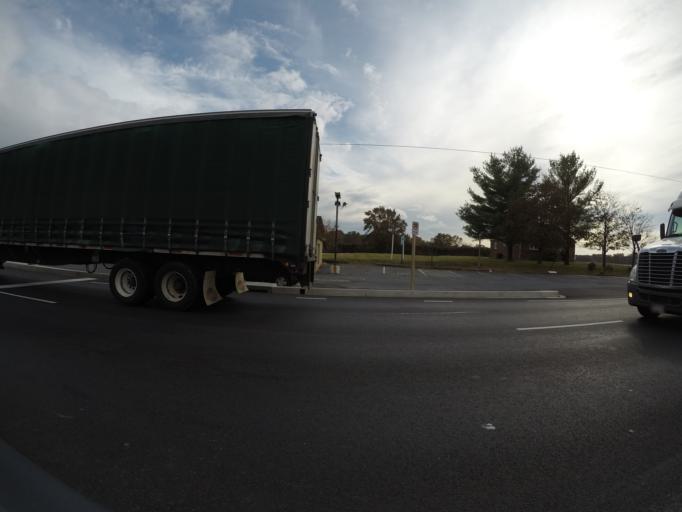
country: US
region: Maryland
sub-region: Harford County
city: Perryman
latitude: 39.4883
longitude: -76.1977
